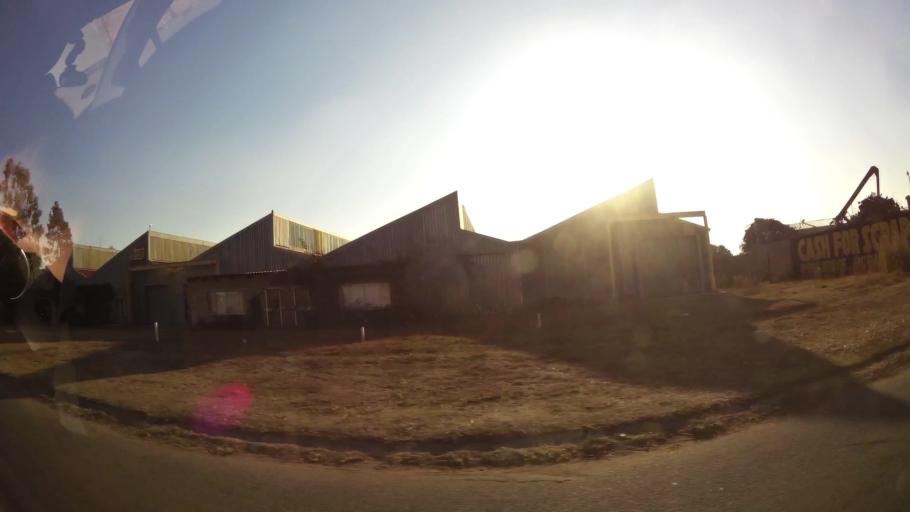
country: ZA
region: Gauteng
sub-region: West Rand District Municipality
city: Randfontein
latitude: -26.2023
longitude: 27.6956
